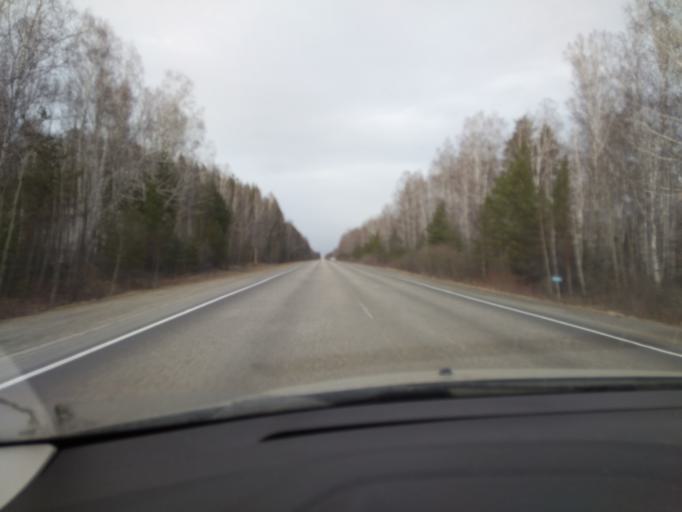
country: RU
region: Chelyabinsk
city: Tyubuk
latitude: 56.0043
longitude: 60.9091
